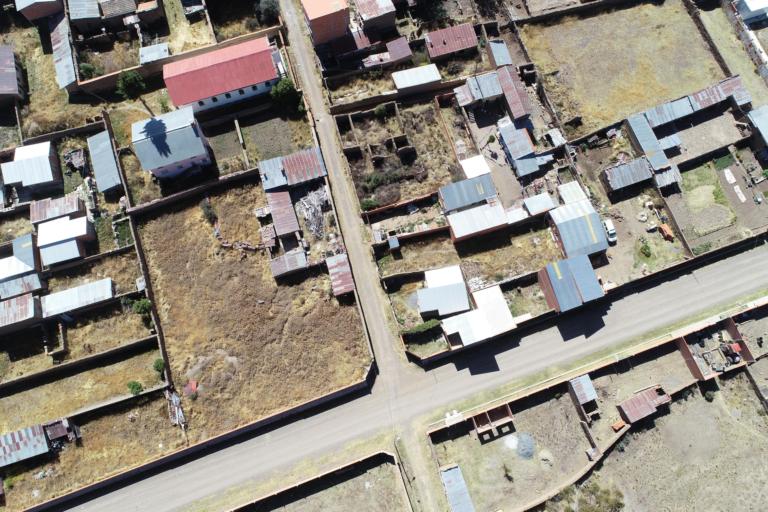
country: BO
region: La Paz
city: Achacachi
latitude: -15.8993
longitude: -68.9053
